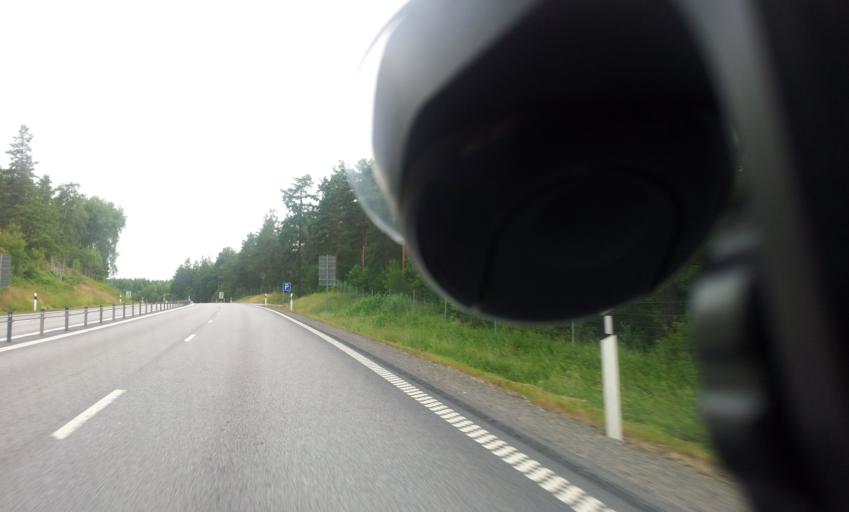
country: SE
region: OEstergoetland
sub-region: Soderkopings Kommun
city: Soederkoeping
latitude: 58.4323
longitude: 16.3816
